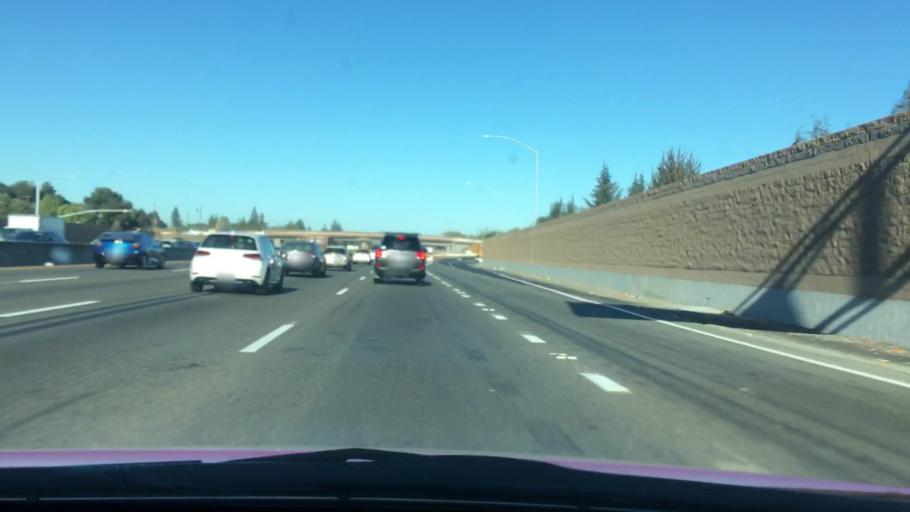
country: US
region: California
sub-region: San Mateo County
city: East Palo Alto
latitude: 37.4670
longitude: -122.1517
